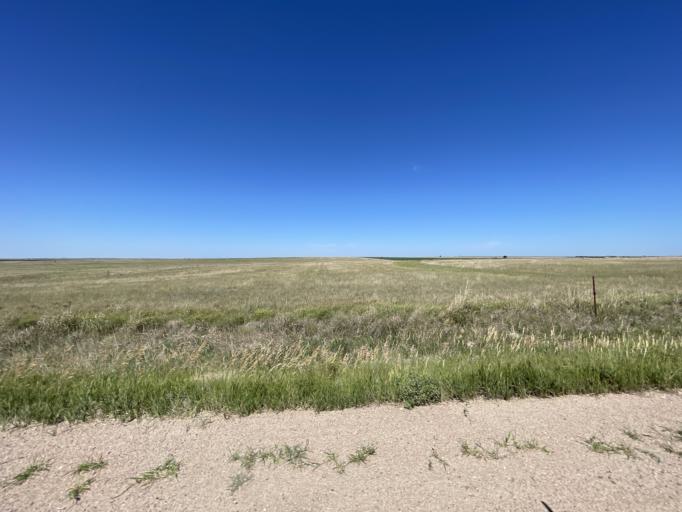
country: US
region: Nebraska
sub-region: Red Willow County
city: McCook
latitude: 40.4367
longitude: -100.7303
